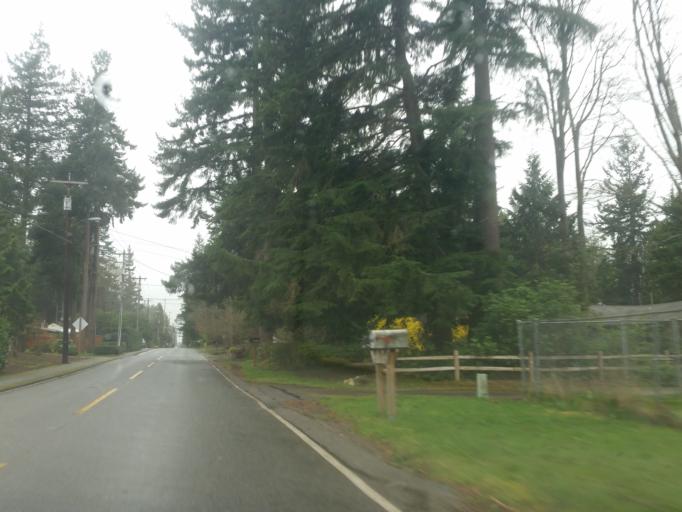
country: US
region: Washington
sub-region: Snohomish County
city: Meadowdale
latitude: 47.8317
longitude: -122.3523
